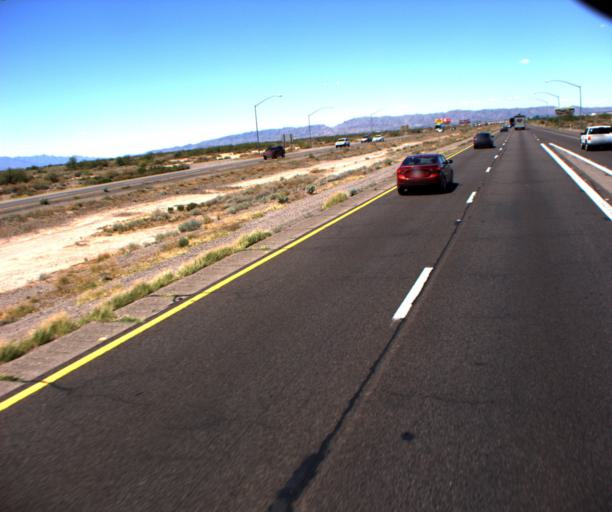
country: US
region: Arizona
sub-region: Maricopa County
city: Sun Lakes
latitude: 33.2218
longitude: -111.9219
